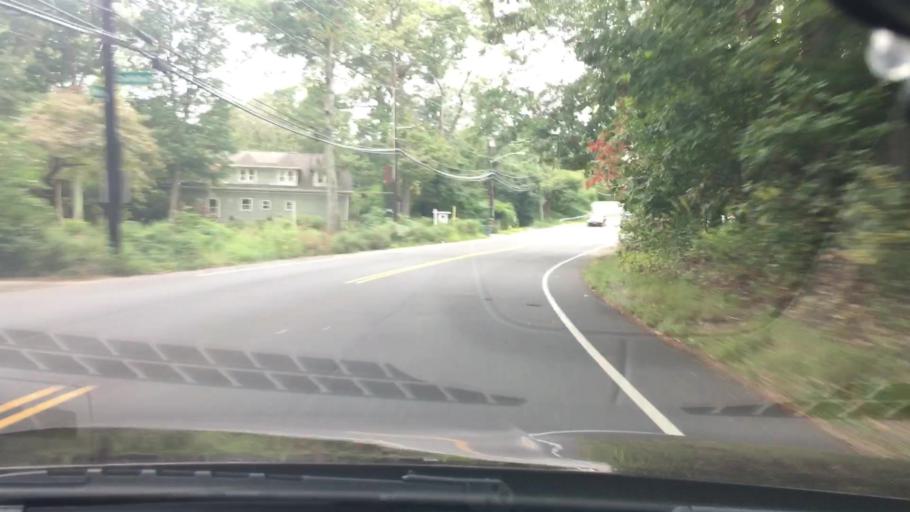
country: US
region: New York
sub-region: Nassau County
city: Bethpage
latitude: 40.7349
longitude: -73.4682
